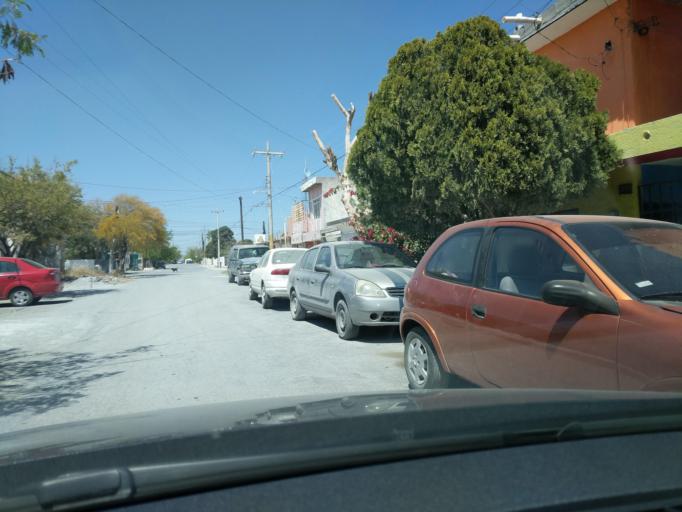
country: MX
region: Nuevo Leon
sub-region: Salinas Victoria
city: Emiliano Zapata
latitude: 25.9128
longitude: -100.2634
